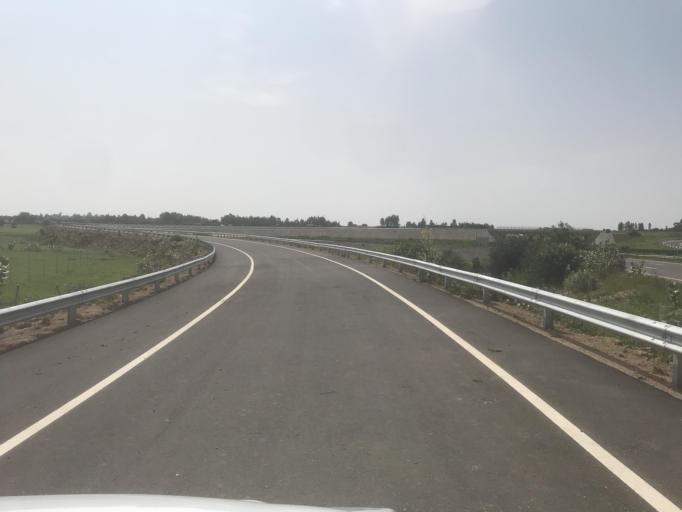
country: ET
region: Oromiya
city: Mojo
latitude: 8.5815
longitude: 39.1709
